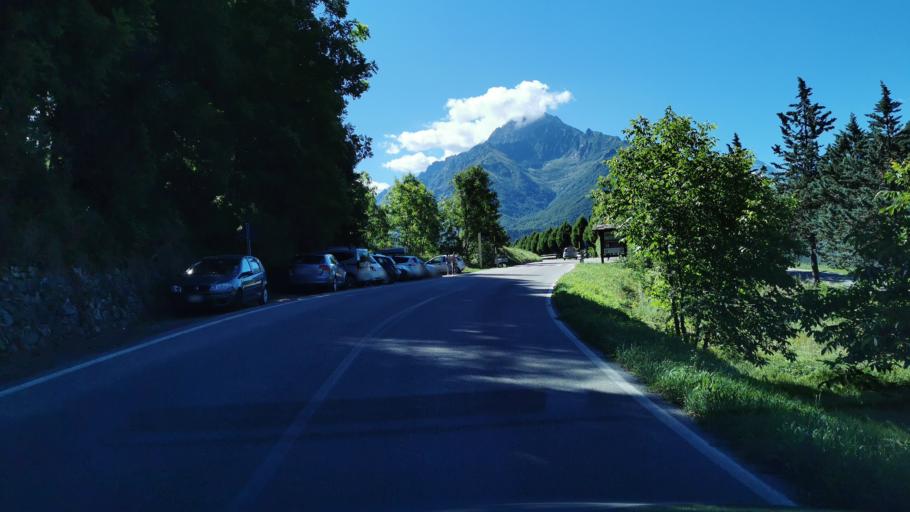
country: IT
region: Piedmont
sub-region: Provincia di Cuneo
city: Entracque
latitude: 44.2517
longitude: 7.3900
